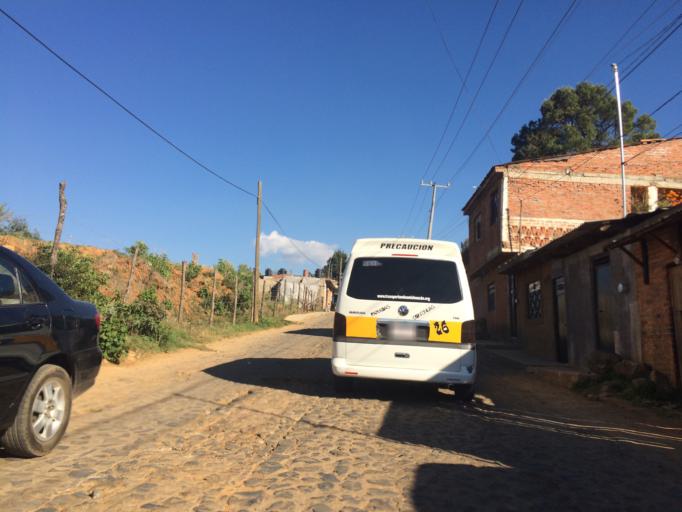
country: MX
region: Michoacan
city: Patzcuaro
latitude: 19.5068
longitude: -101.5971
